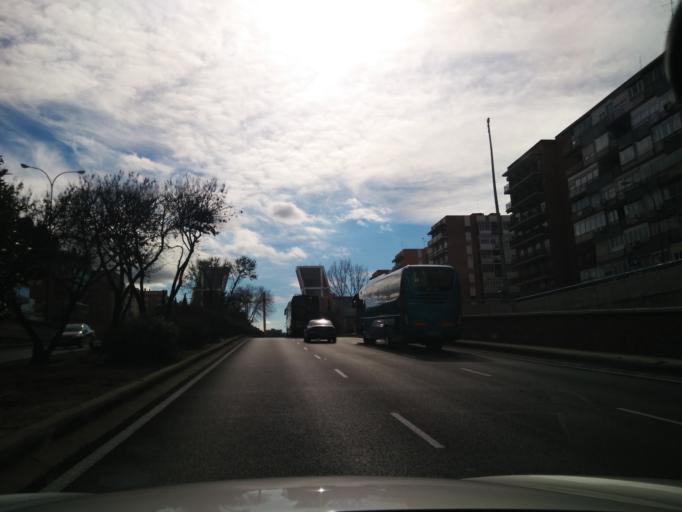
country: ES
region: Madrid
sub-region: Provincia de Madrid
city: Chamartin
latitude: 40.4739
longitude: -3.6873
